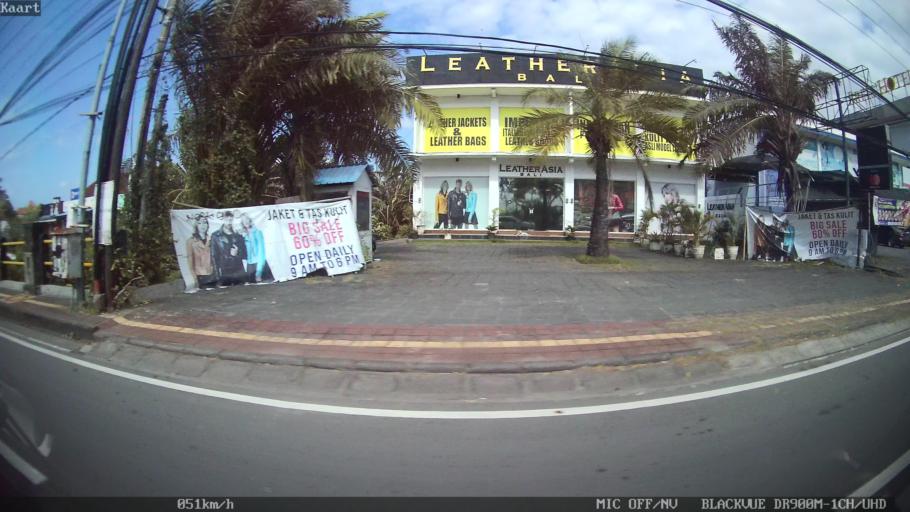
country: ID
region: Bali
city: Kuta
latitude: -8.6971
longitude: 115.1768
